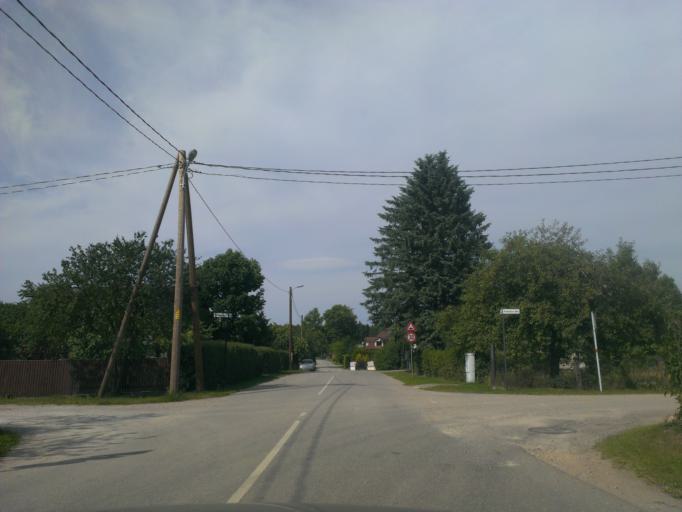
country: LV
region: Baldone
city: Baldone
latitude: 56.7459
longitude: 24.3906
